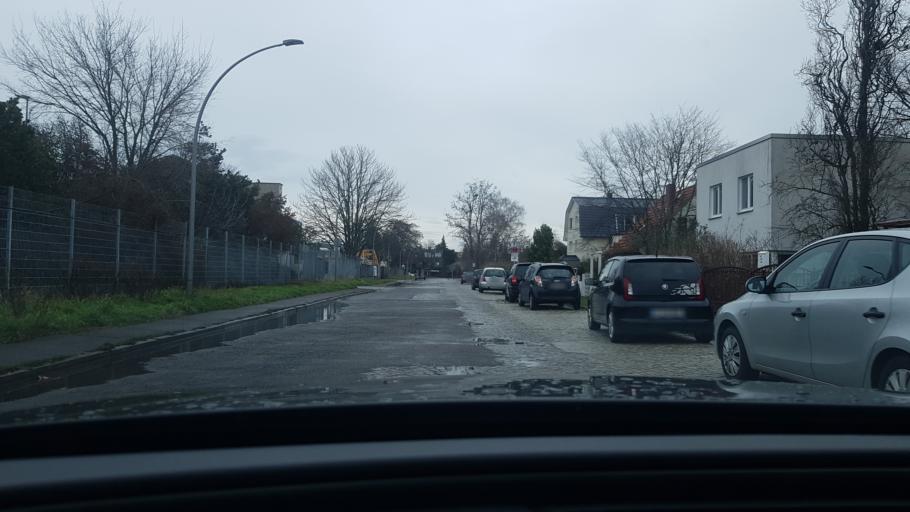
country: DE
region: Berlin
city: Marienfelde
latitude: 52.4202
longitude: 13.3830
